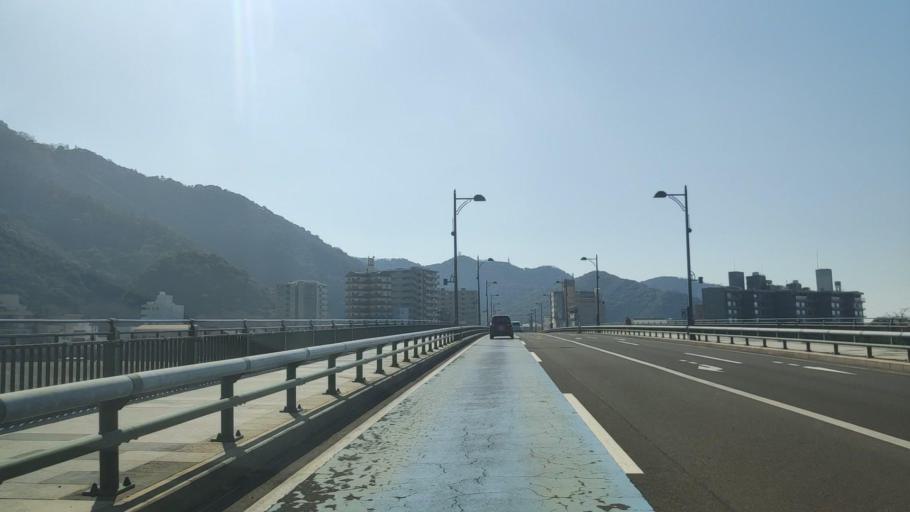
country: JP
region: Gifu
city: Gifu-shi
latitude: 35.4407
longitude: 136.7736
